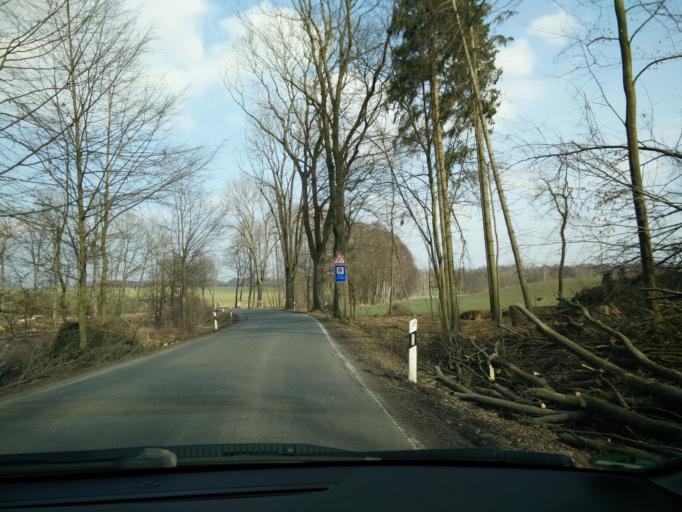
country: DE
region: Saxony
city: Colditz
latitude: 51.1054
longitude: 12.7720
